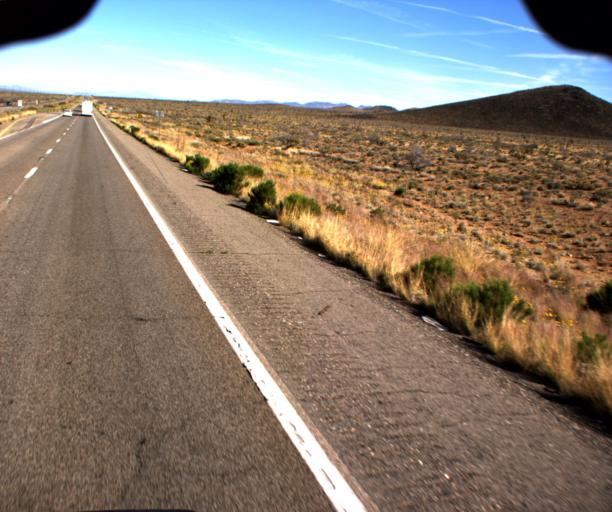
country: US
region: Arizona
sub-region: Mohave County
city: Dolan Springs
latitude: 35.4547
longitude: -114.3004
